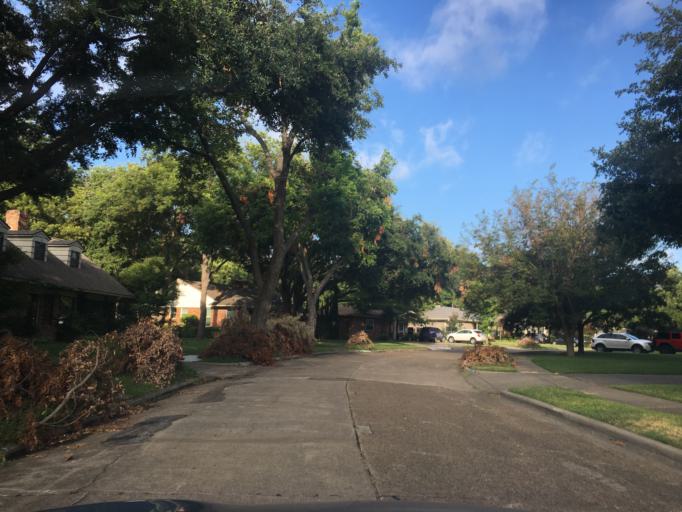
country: US
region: Texas
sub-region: Dallas County
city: Highland Park
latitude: 32.8483
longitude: -96.7504
